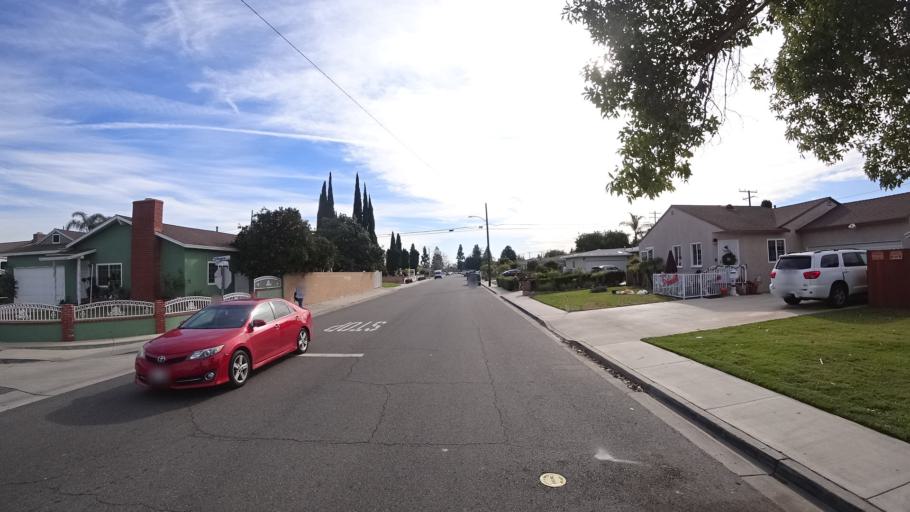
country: US
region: California
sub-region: Orange County
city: Garden Grove
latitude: 33.7696
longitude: -117.9069
